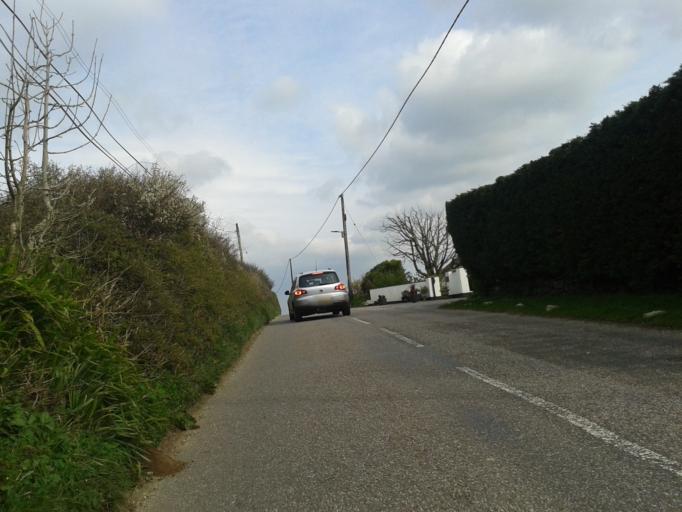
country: GB
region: England
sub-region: Devon
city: Braunton
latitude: 51.1764
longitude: -4.1752
